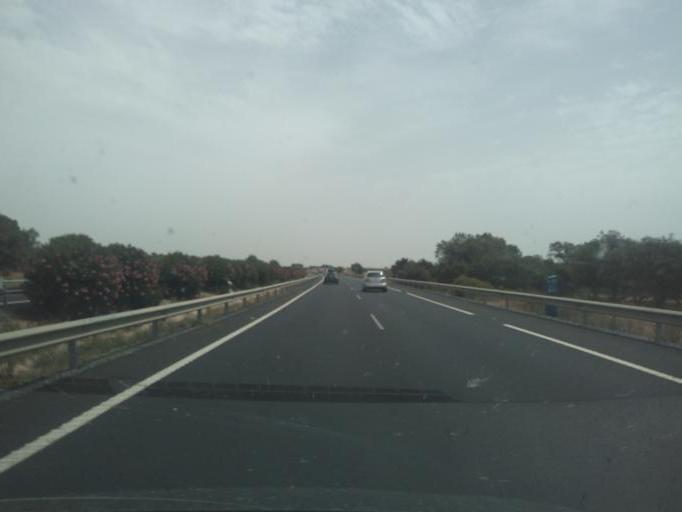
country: ES
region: Andalusia
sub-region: Provincia de Huelva
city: Manzanilla
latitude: 37.3464
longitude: -6.4578
